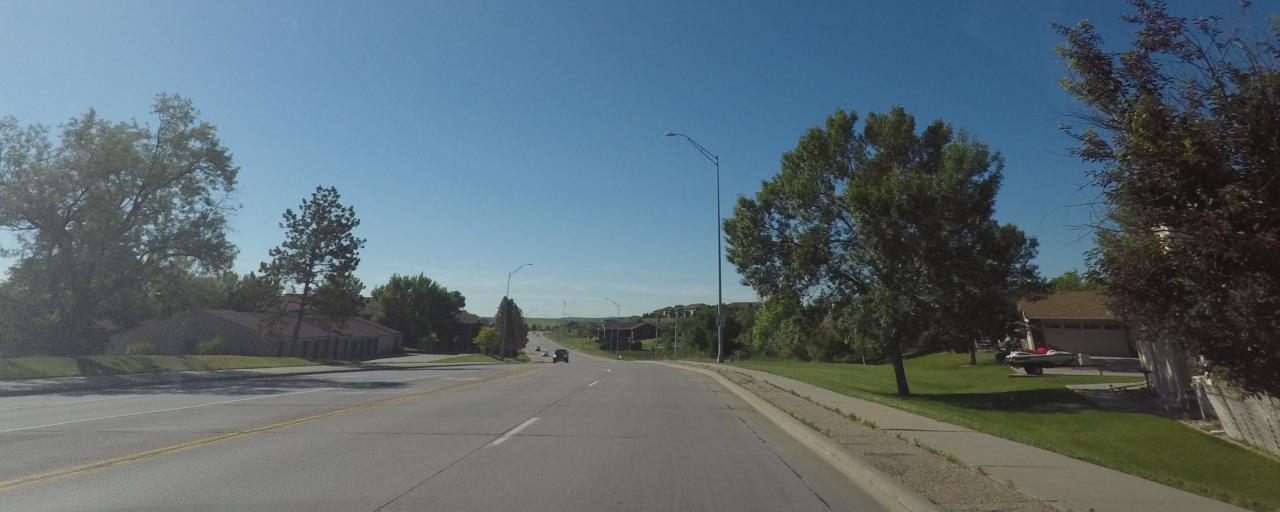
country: US
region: South Dakota
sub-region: Pennington County
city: Rapid City
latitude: 44.0491
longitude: -103.2237
